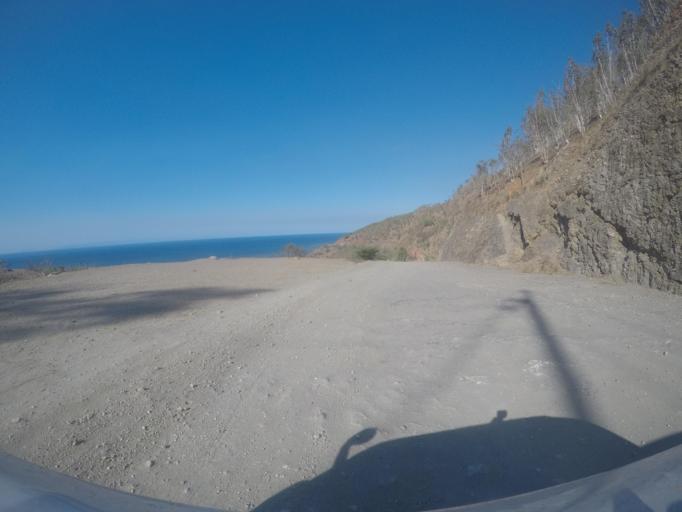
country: TL
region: Dili
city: Dili
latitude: -8.5298
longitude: 125.6206
